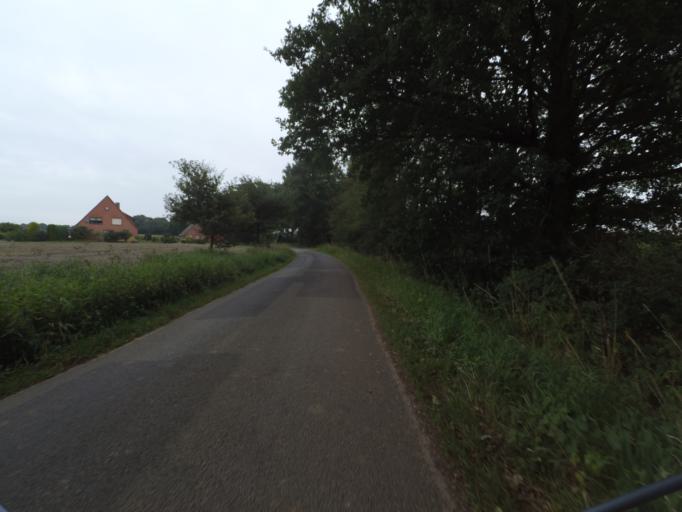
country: DE
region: Lower Saxony
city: Isterberg
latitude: 52.3347
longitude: 7.0630
